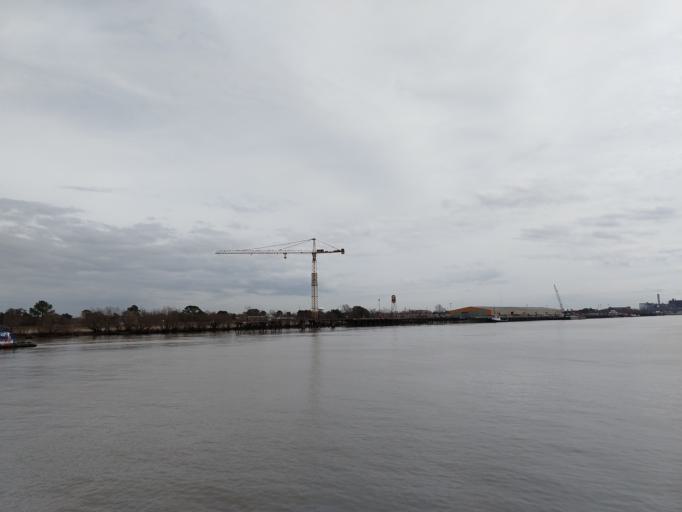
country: US
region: Louisiana
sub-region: Saint Bernard Parish
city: Arabi
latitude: 29.9536
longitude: -90.0253
